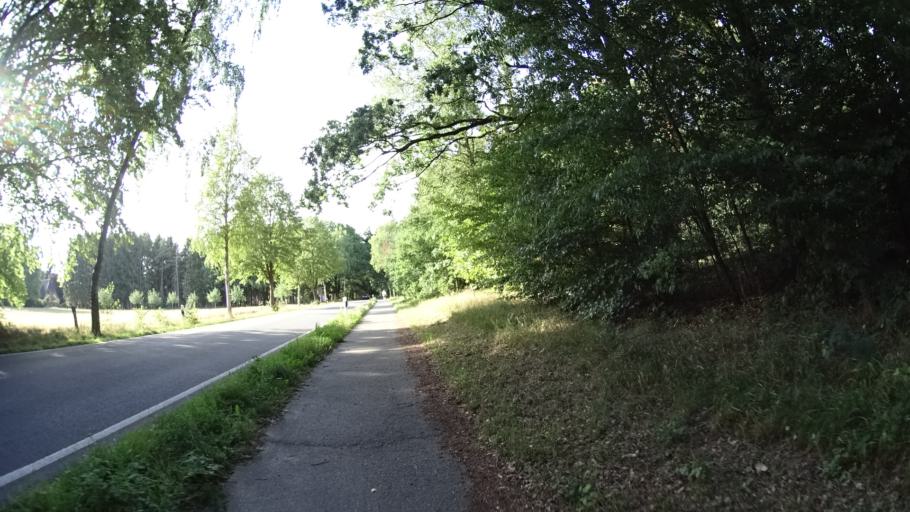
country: DE
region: Lower Saxony
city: Undeloh
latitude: 53.1524
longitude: 9.9071
